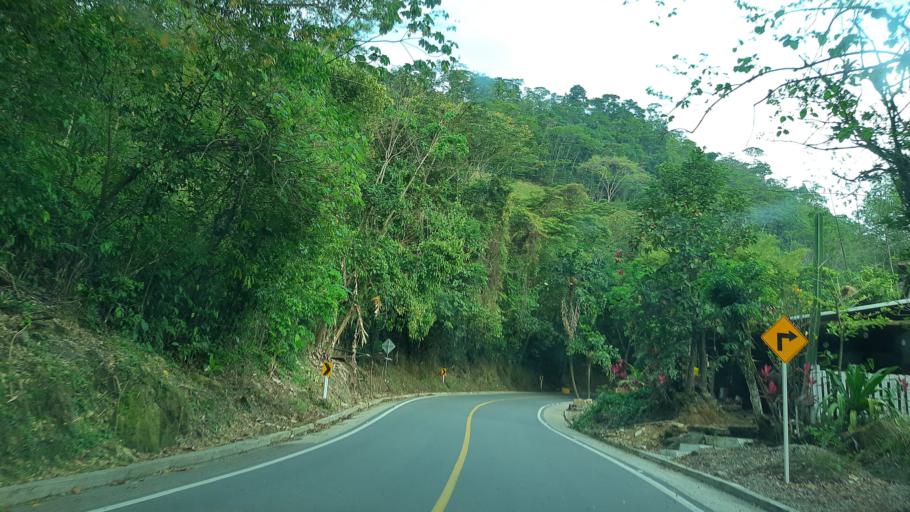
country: CO
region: Boyaca
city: San Luis de Gaceno
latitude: 4.8390
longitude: -73.2148
